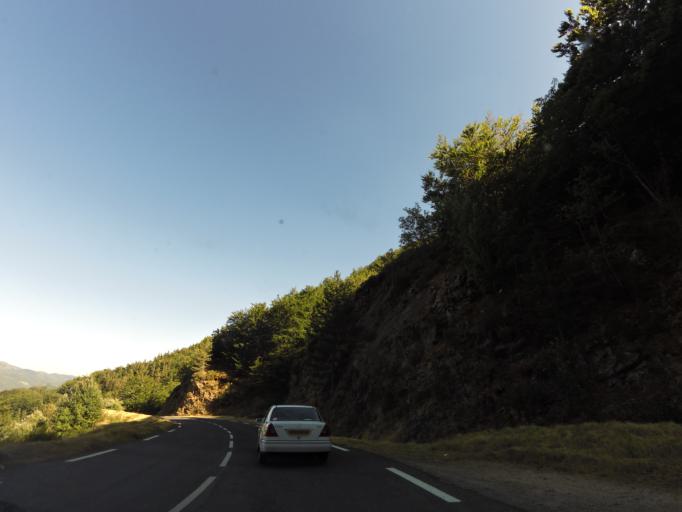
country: FR
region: Languedoc-Roussillon
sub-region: Departement du Gard
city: Valleraugue
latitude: 44.0864
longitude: 3.5755
